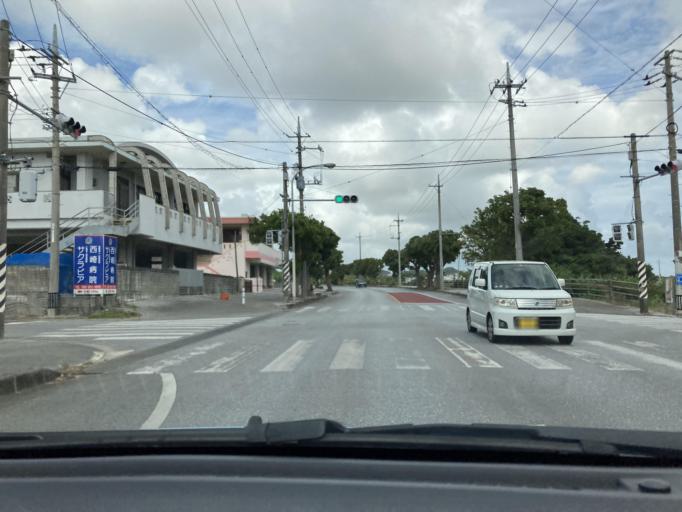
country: JP
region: Okinawa
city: Itoman
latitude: 26.1423
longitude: 127.6926
